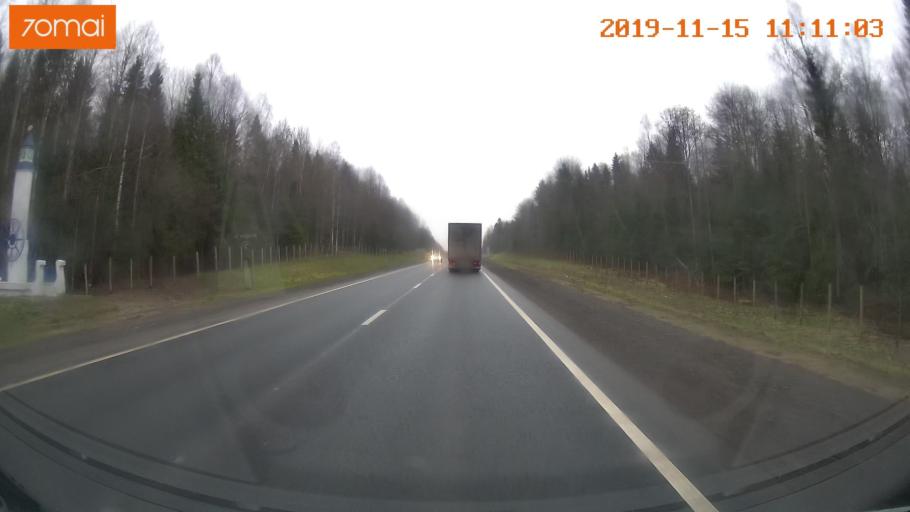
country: RU
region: Vologda
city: Chebsara
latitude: 59.1212
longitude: 39.1343
